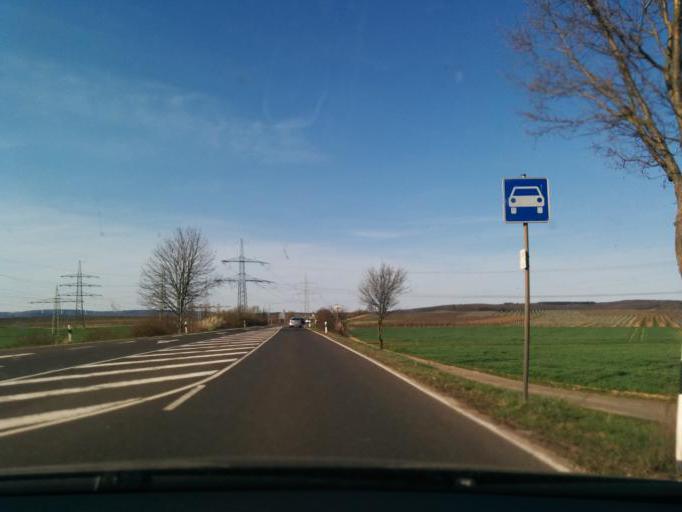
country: DE
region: Rheinland-Pfalz
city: Windesheim
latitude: 49.8892
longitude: 7.8183
